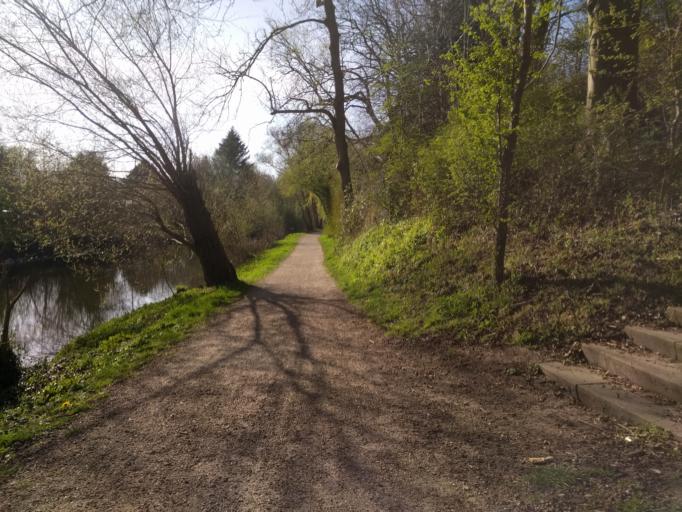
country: DK
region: South Denmark
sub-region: Odense Kommune
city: Seden
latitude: 55.4013
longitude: 10.4378
